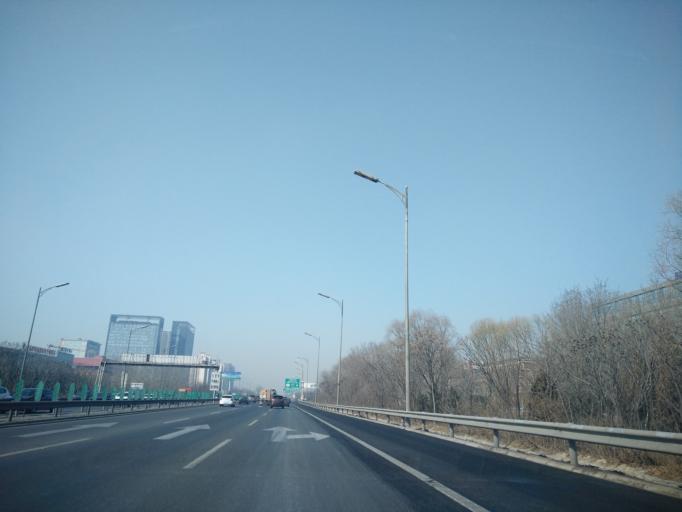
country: CN
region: Beijing
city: Wangjing
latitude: 40.0139
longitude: 116.4716
